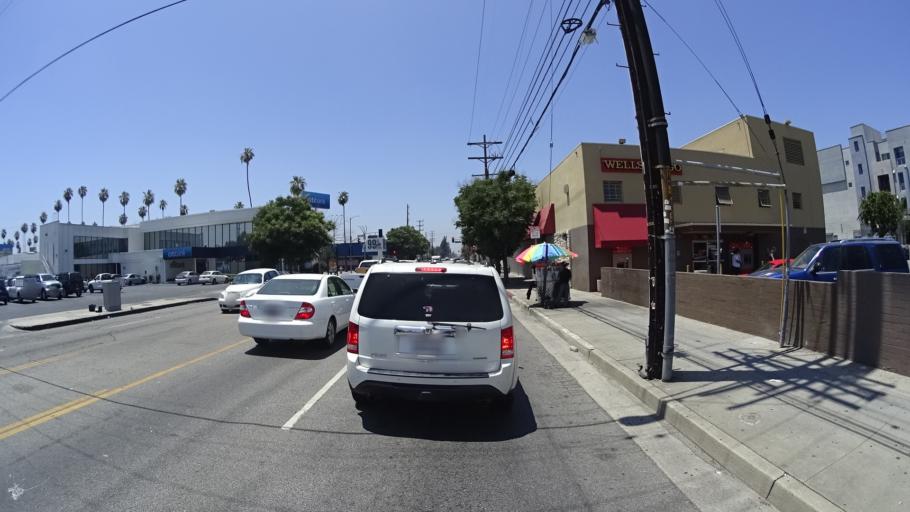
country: US
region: California
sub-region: Los Angeles County
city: Van Nuys
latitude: 34.1940
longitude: -118.4477
